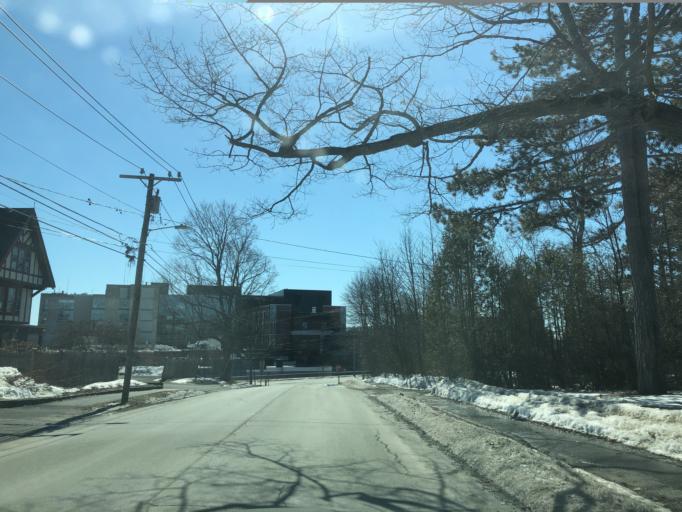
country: US
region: Maine
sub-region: Penobscot County
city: Brewer
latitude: 44.8101
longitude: -68.7522
